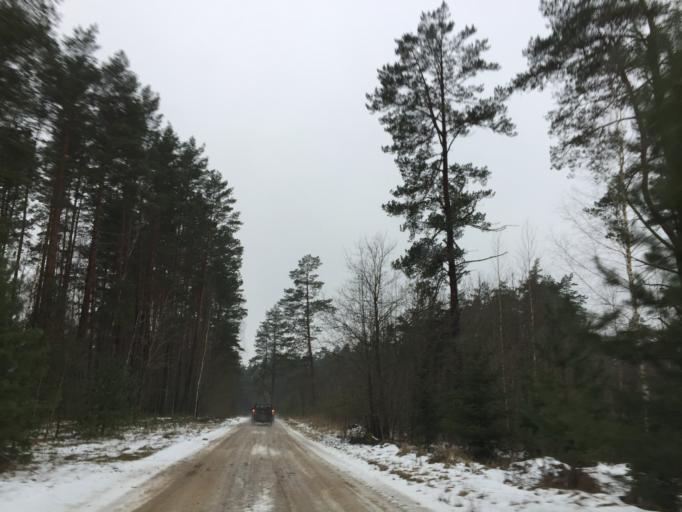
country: LV
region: Incukalns
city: Vangazi
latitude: 57.1293
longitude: 24.5765
